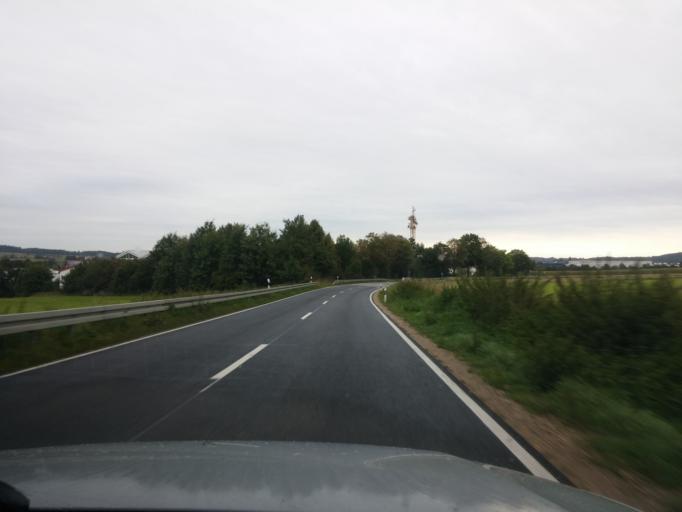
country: DE
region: Bavaria
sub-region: Upper Bavaria
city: Allershausen
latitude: 48.4271
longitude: 11.5692
